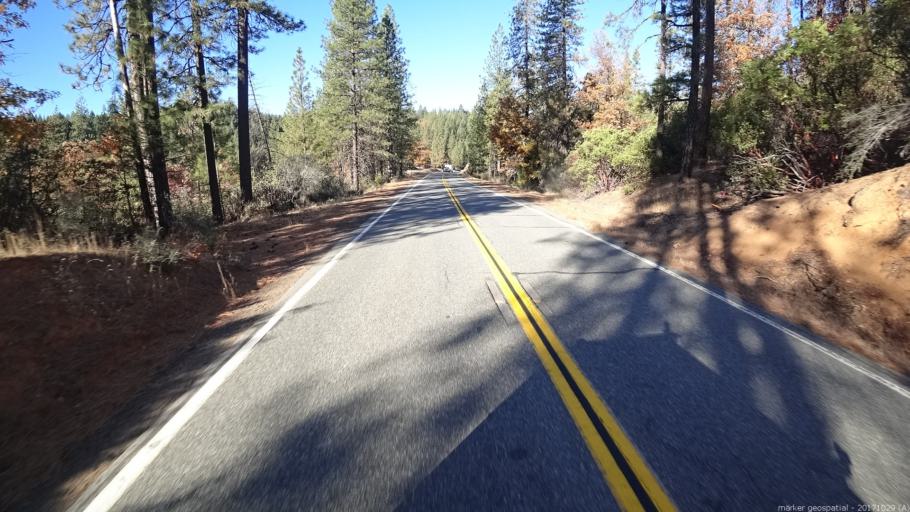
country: US
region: California
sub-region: Trinity County
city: Hayfork
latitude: 40.3634
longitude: -122.9632
